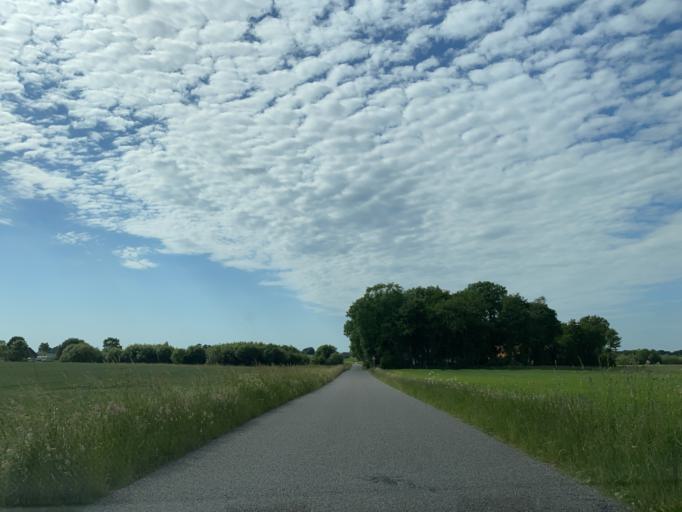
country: DK
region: Central Jutland
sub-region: Favrskov Kommune
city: Hammel
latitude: 56.2126
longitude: 9.8930
